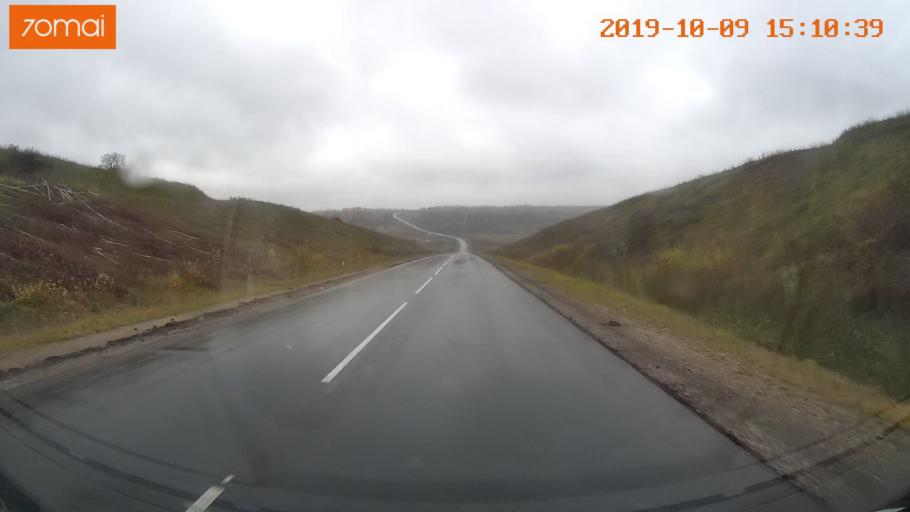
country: RU
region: Kostroma
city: Susanino
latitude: 58.1752
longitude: 41.6375
